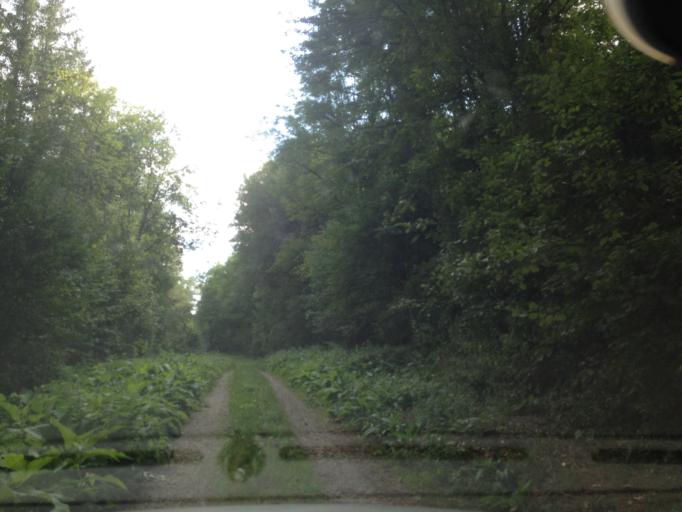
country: FR
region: Franche-Comte
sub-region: Departement de la Haute-Saone
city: Saint-Loup-sur-Semouse
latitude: 47.8314
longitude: 6.2098
